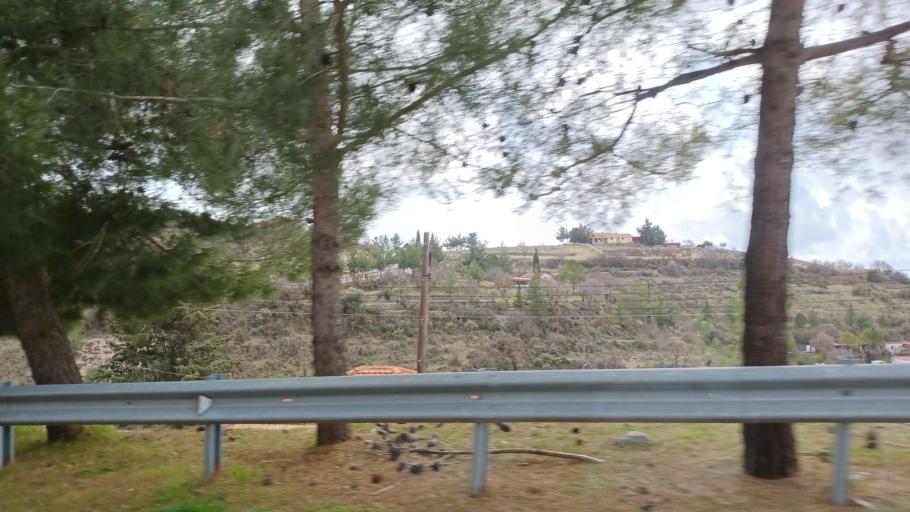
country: CY
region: Limassol
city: Pachna
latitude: 34.8399
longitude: 32.7714
